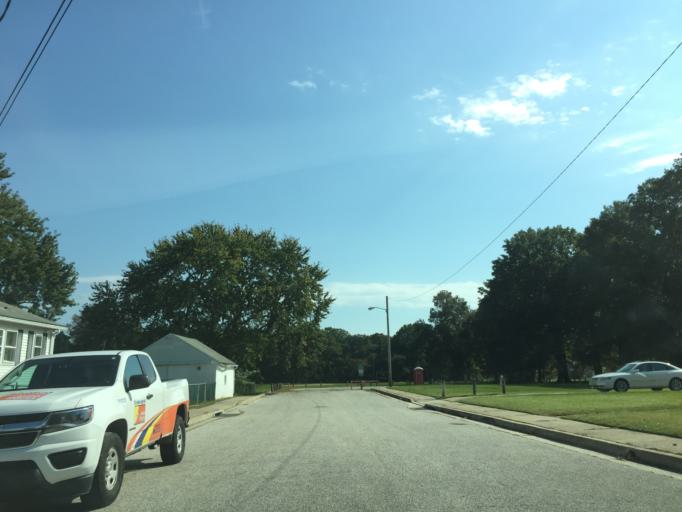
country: US
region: Maryland
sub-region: Baltimore County
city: Essex
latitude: 39.3072
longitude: -76.4571
